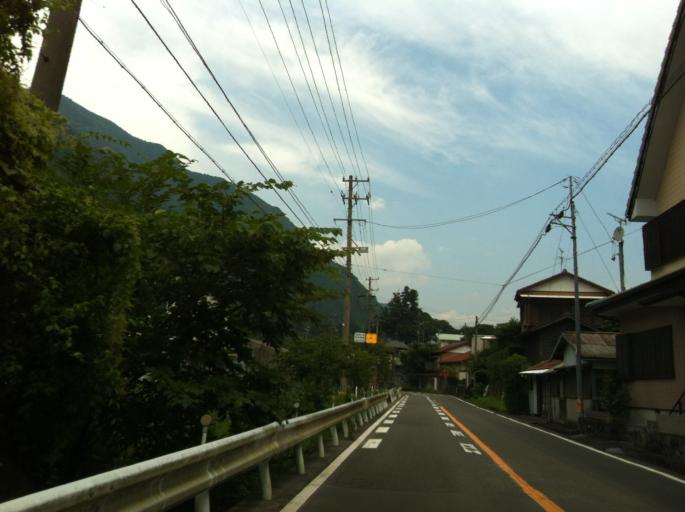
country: JP
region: Shizuoka
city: Shizuoka-shi
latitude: 35.1450
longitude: 138.3655
